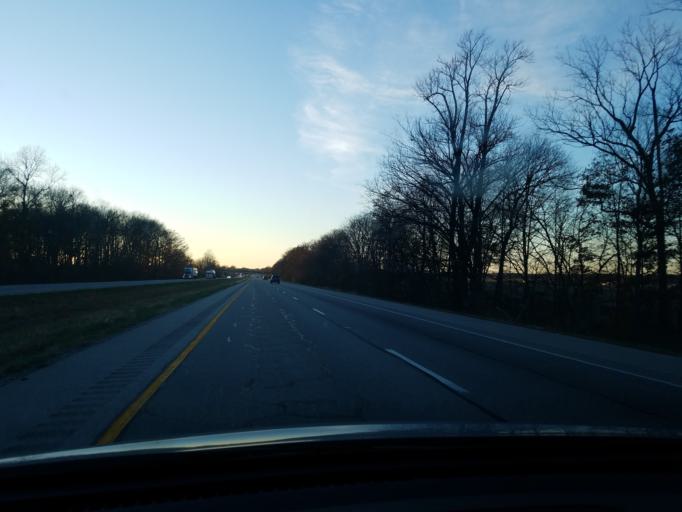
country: US
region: Indiana
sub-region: Posey County
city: Poseyville
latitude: 38.1844
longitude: -87.8021
